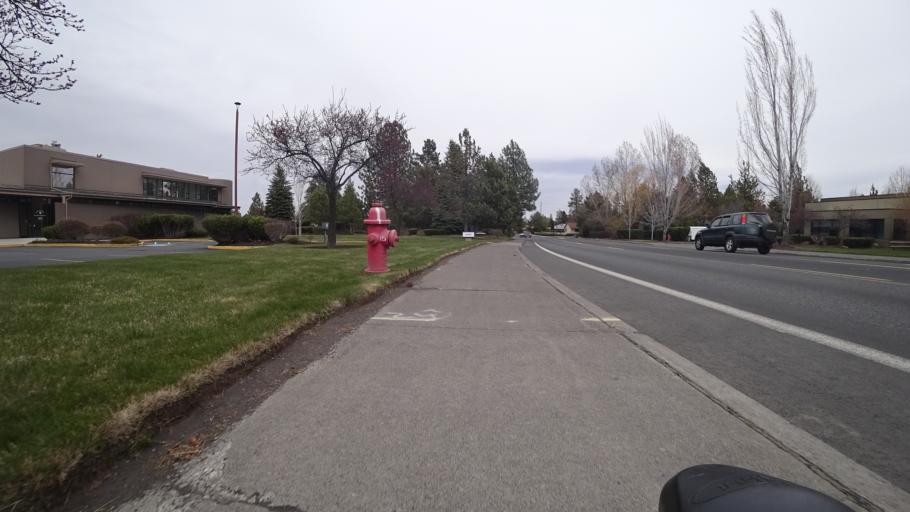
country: US
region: Oregon
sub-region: Deschutes County
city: Bend
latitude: 44.0443
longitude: -121.2870
